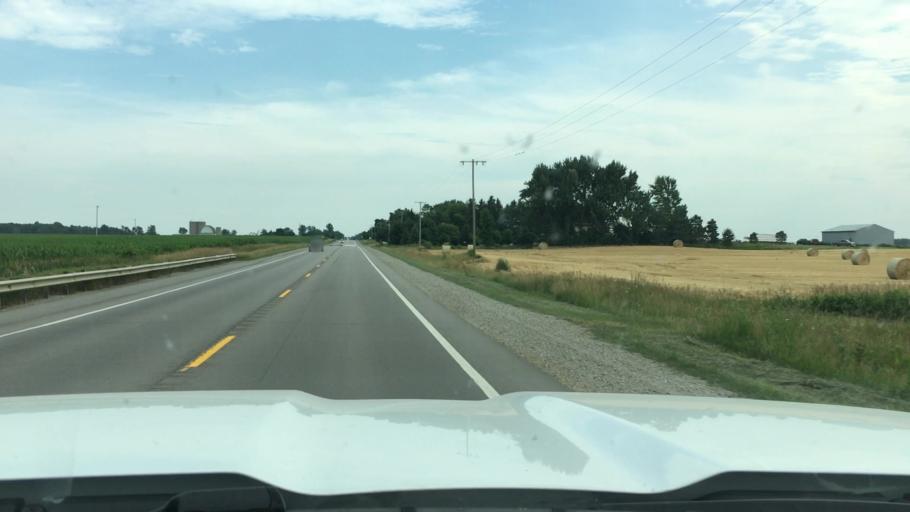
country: US
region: Michigan
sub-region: Sanilac County
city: Marlette
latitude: 43.3678
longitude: -83.0854
